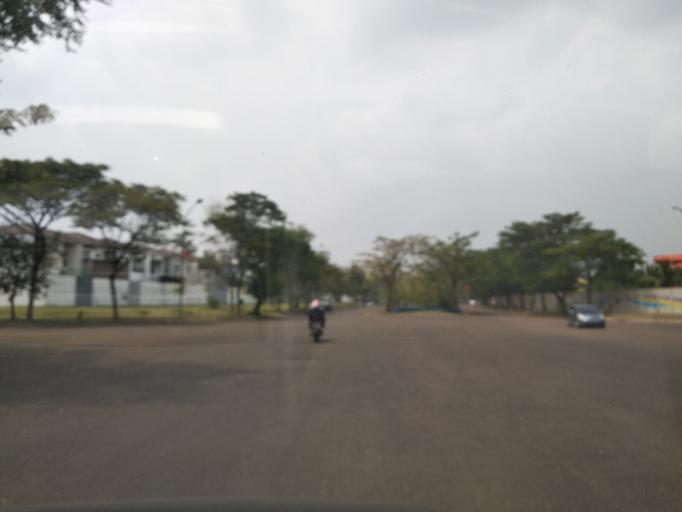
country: ID
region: West Java
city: Bekasi
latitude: -6.2958
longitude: 107.0503
